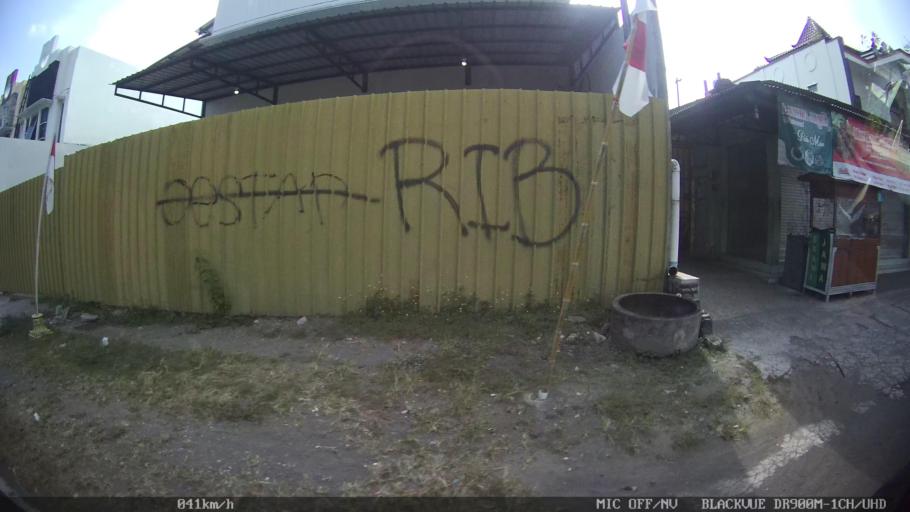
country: ID
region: Daerah Istimewa Yogyakarta
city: Depok
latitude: -7.7290
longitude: 110.4349
